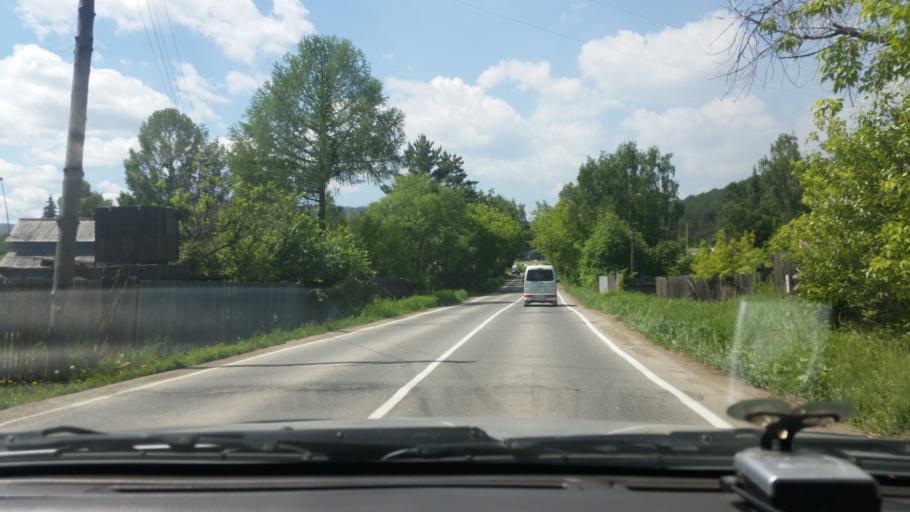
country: RU
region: Irkutsk
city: Shelekhov
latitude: 52.1516
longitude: 104.0740
